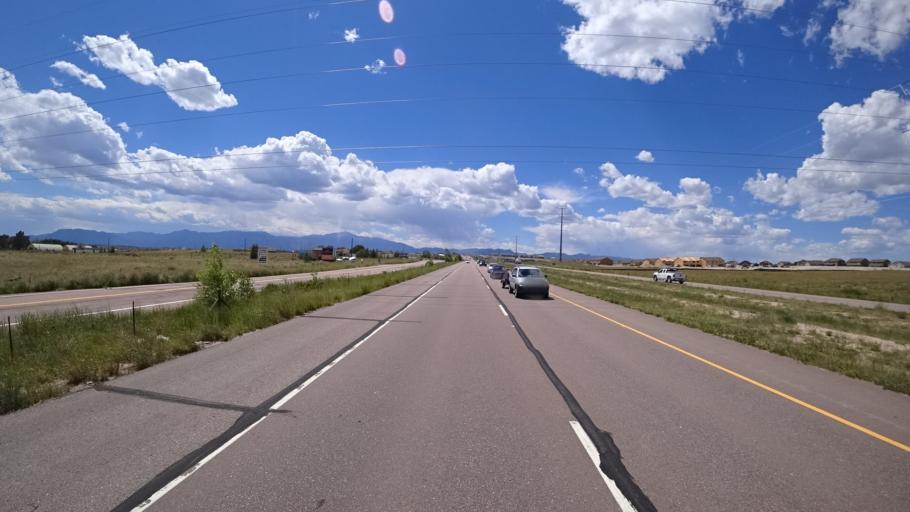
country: US
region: Colorado
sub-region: El Paso County
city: Black Forest
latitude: 38.9411
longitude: -104.6866
